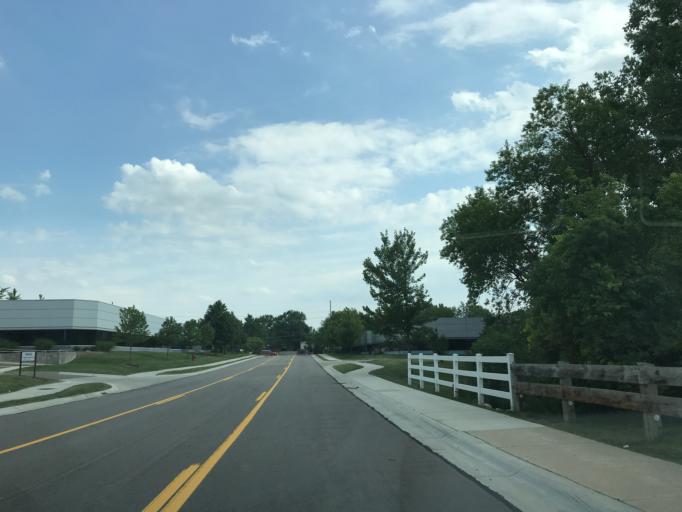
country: US
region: Michigan
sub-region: Oakland County
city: Novi
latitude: 42.4697
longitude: -83.4390
